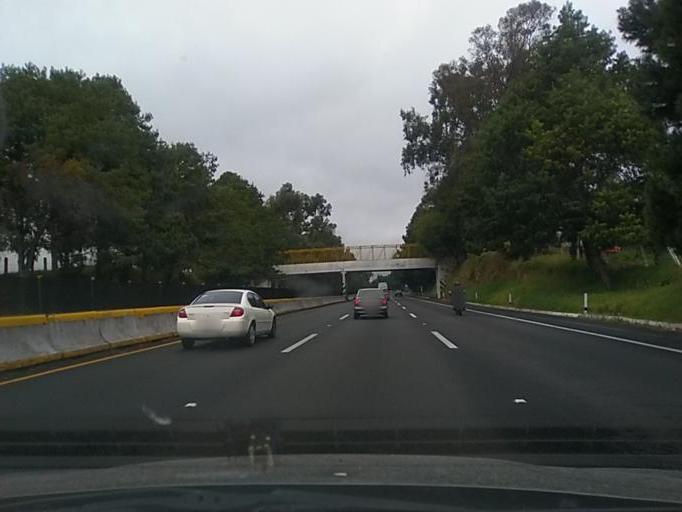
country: MX
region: Mexico City
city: Xochimilco
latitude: 19.1887
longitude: -99.1581
